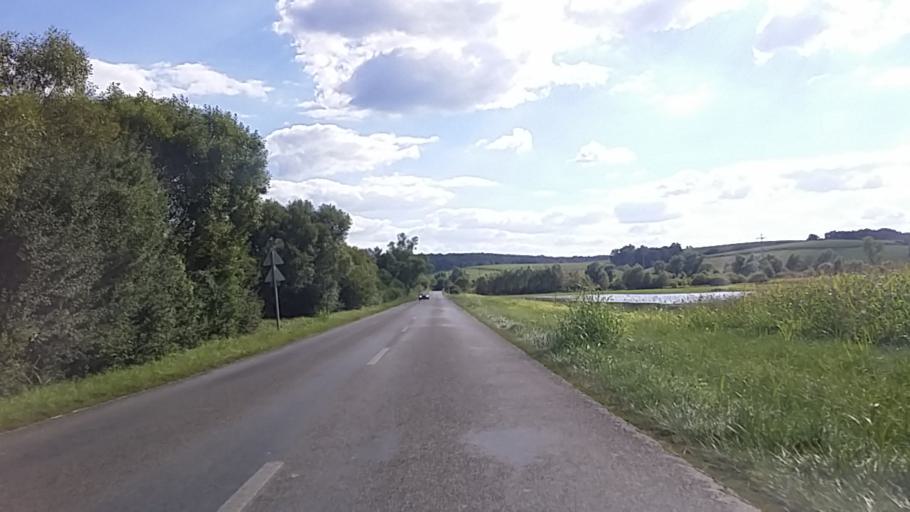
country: HU
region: Baranya
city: Sasd
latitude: 46.2196
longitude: 18.1094
